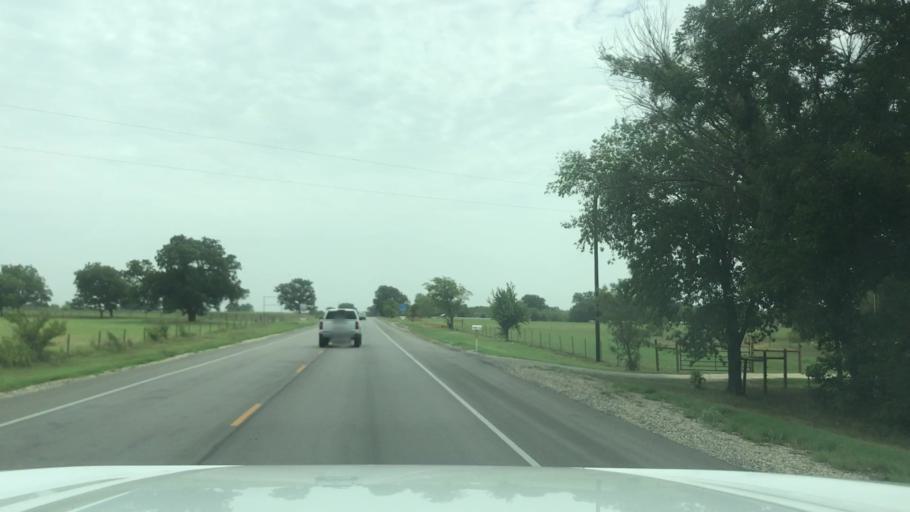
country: US
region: Texas
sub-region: Erath County
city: Dublin
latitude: 32.0899
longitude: -98.2860
